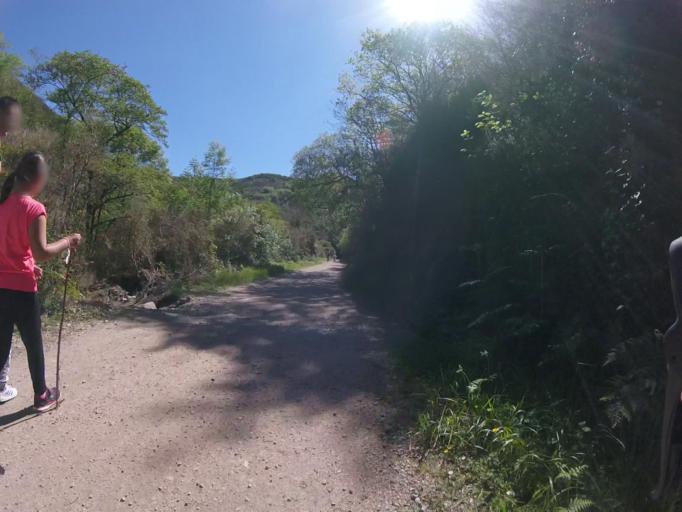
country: ES
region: Navarre
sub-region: Provincia de Navarra
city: Bera
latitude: 43.2907
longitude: -1.7162
